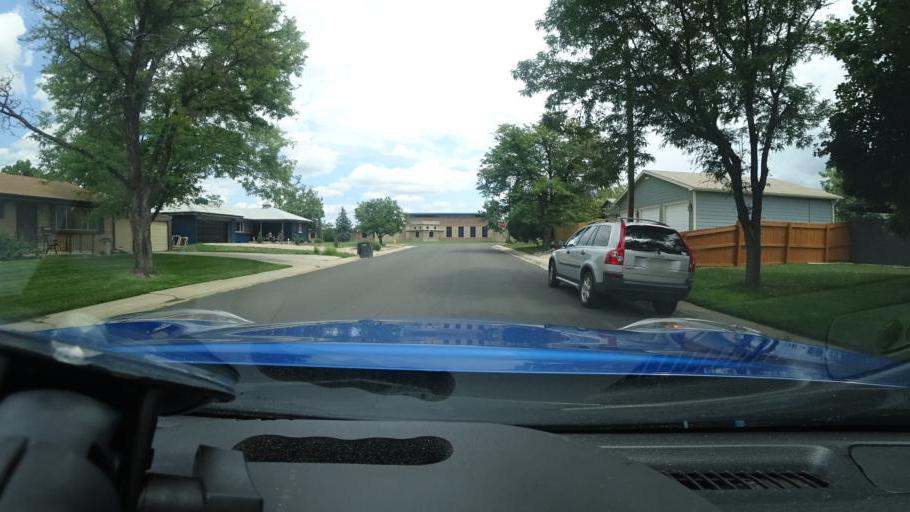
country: US
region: Colorado
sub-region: Adams County
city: Aurora
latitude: 39.7242
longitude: -104.8320
